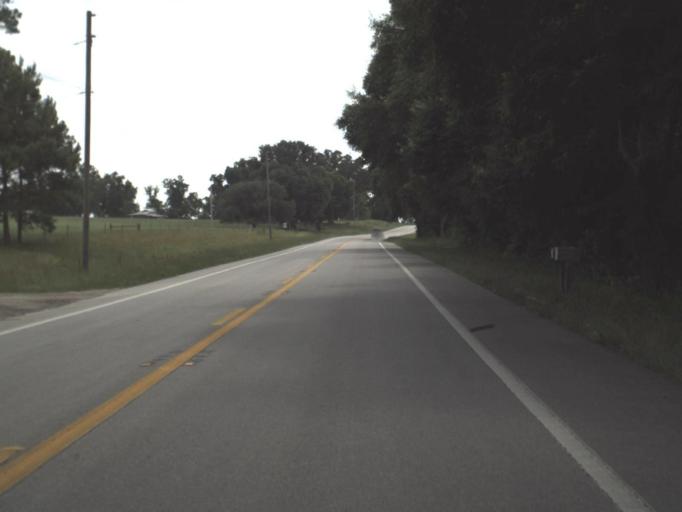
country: US
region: Florida
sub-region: Madison County
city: Madison
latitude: 30.5154
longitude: -83.4226
